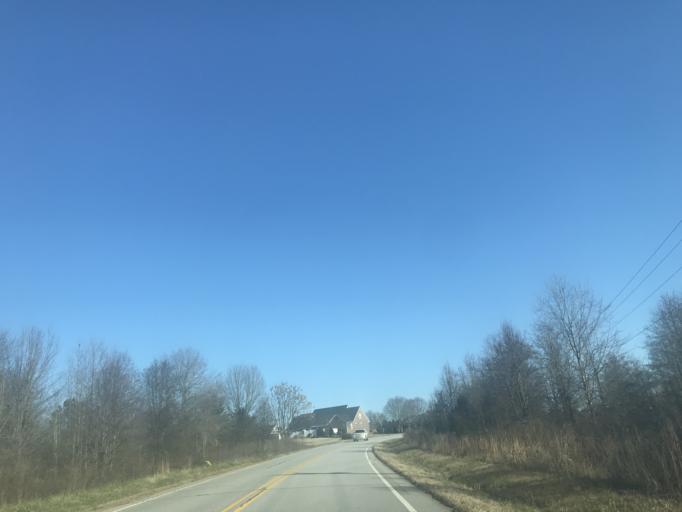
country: US
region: South Carolina
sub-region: Cherokee County
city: Gaffney
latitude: 35.1197
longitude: -81.6911
